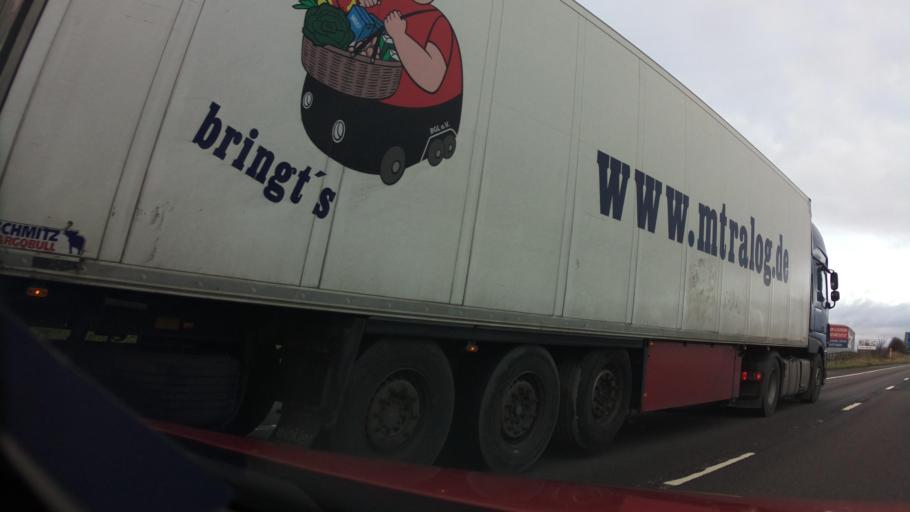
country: GB
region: England
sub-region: Staffordshire
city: Audley
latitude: 53.0595
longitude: -2.3321
